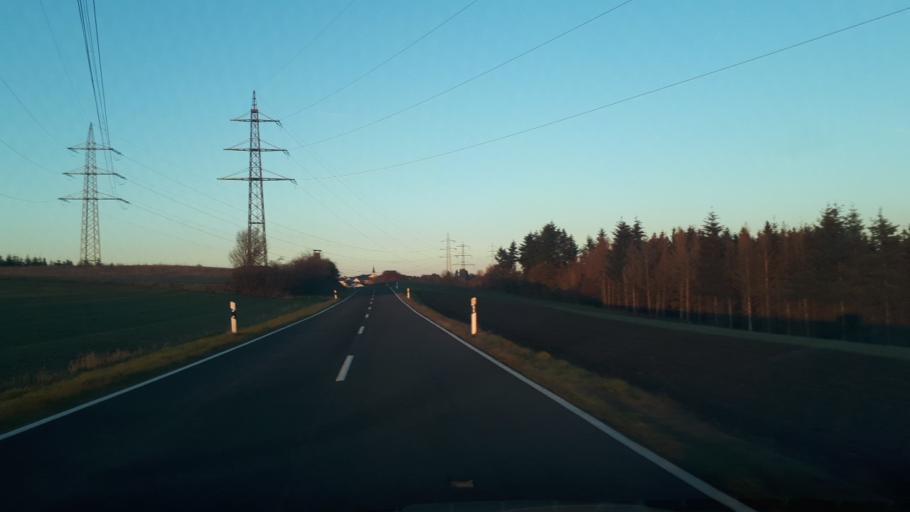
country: DE
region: Rheinland-Pfalz
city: Beuren
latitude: 50.0862
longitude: 7.0740
